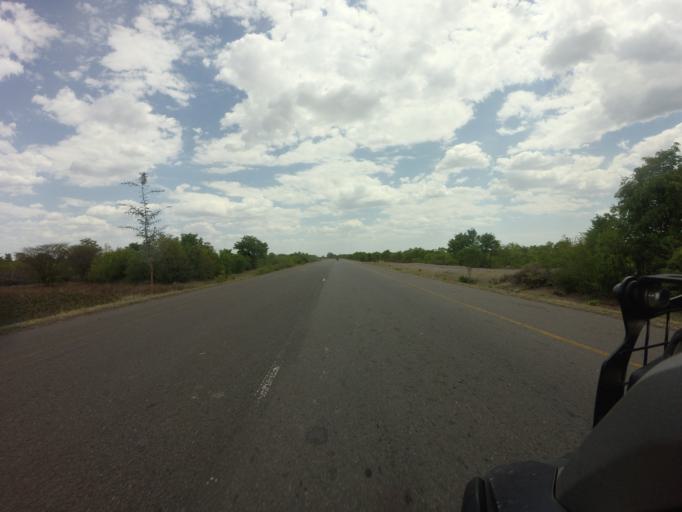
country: AO
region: Huila
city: Lubango
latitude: -15.5652
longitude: 14.0511
